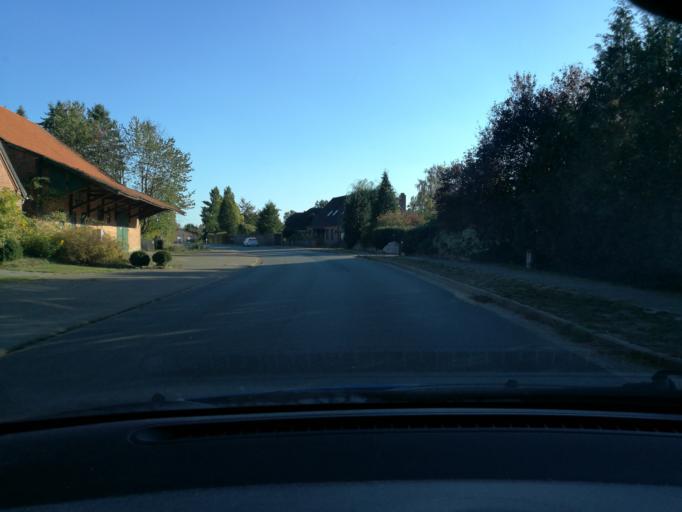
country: DE
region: Lower Saxony
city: Hittbergen
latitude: 53.3232
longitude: 10.5976
